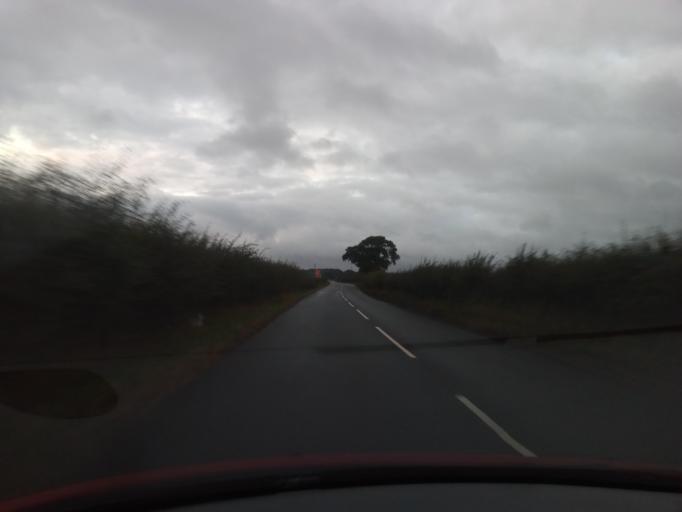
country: GB
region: England
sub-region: Darlington
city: Denton
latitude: 54.5617
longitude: -1.6762
